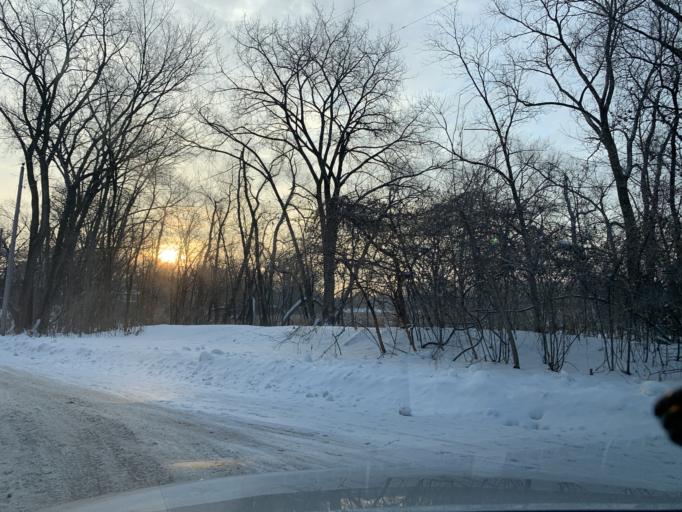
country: US
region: Minnesota
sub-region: Hennepin County
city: Saint Louis Park
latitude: 44.9240
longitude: -93.3593
